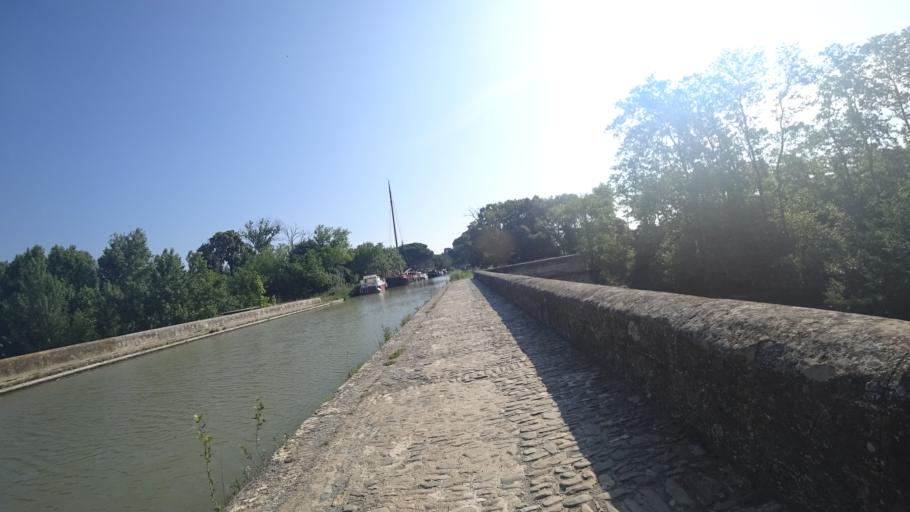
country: FR
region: Languedoc-Roussillon
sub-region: Departement de l'Aude
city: Argeliers
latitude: 43.2800
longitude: 2.9155
